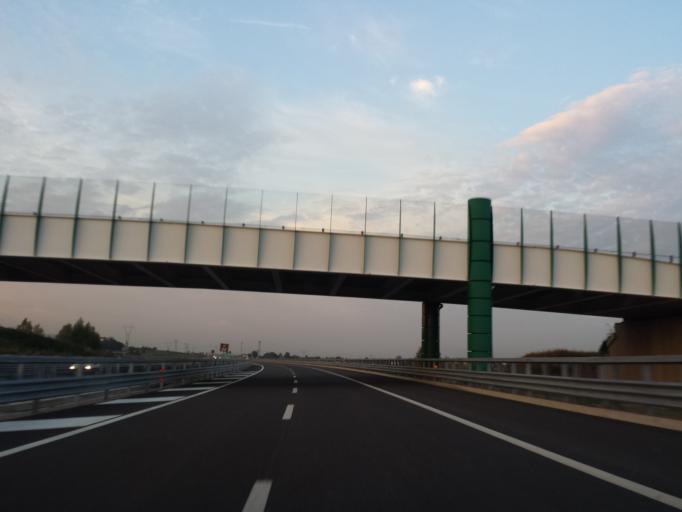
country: IT
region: Veneto
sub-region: Provincia di Vicenza
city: Albettone
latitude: 45.3645
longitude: 11.6086
